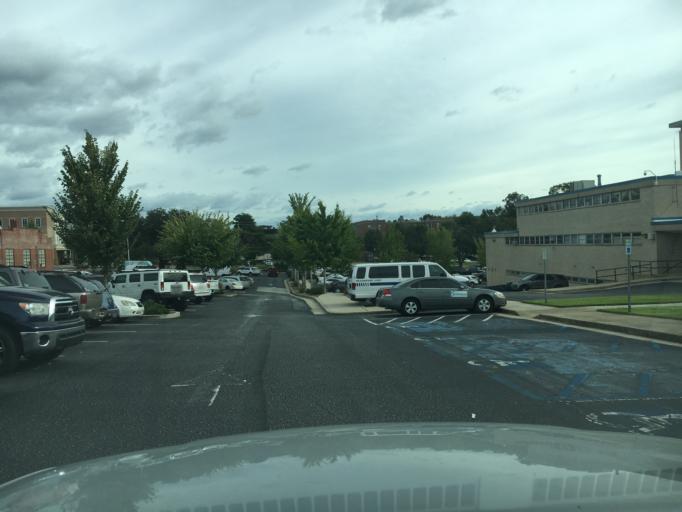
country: US
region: South Carolina
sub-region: Spartanburg County
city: Spartanburg
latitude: 34.9484
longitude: -81.9322
